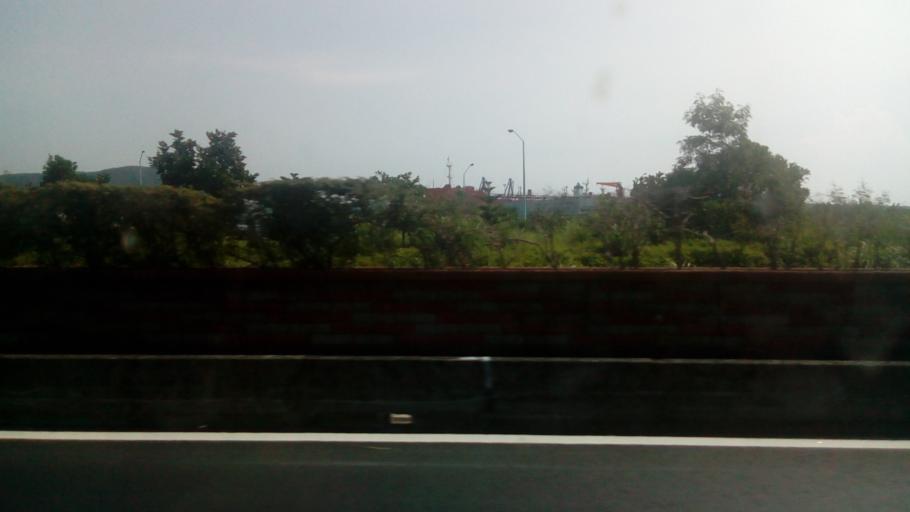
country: TW
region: Taiwan
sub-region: Yilan
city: Yilan
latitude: 24.5941
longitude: 121.8582
